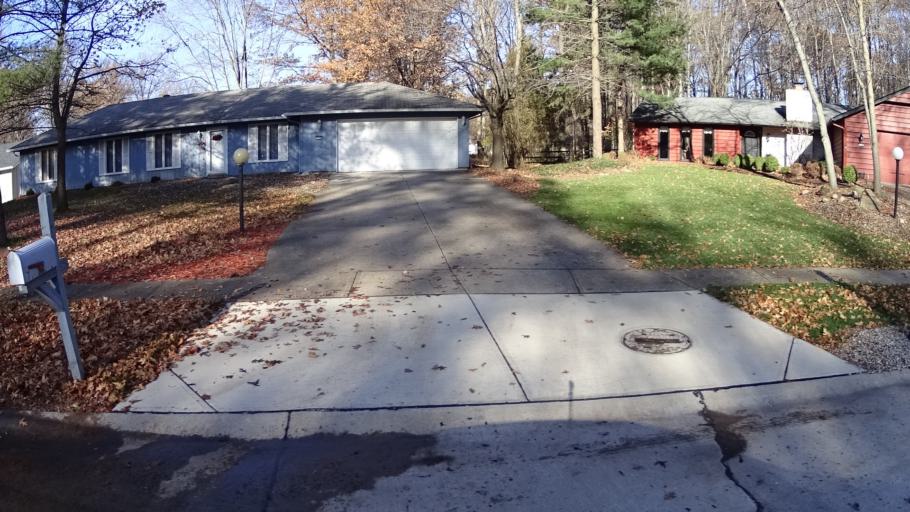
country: US
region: Ohio
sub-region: Lorain County
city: North Ridgeville
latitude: 41.4055
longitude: -81.9733
